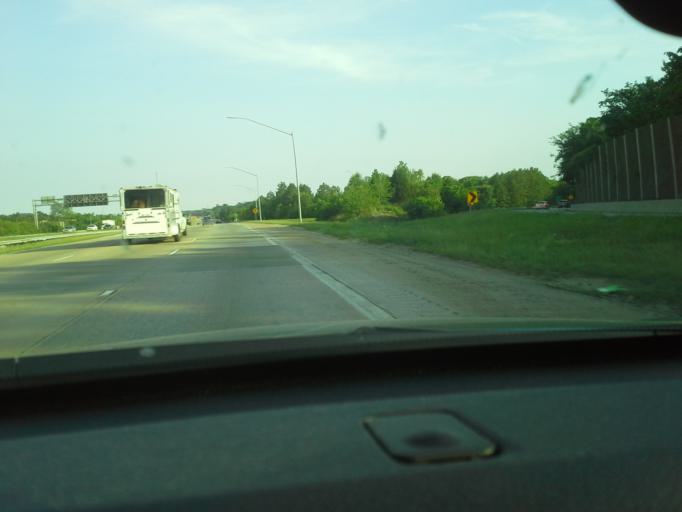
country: US
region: Maryland
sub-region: Anne Arundel County
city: South Gate
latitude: 39.1302
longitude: -76.6426
